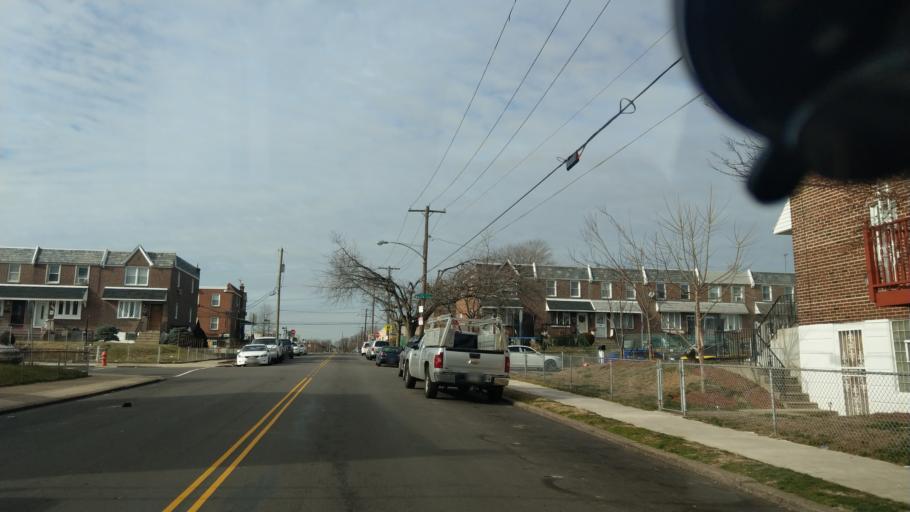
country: US
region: Pennsylvania
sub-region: Montgomery County
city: Rockledge
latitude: 40.0132
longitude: -75.1082
